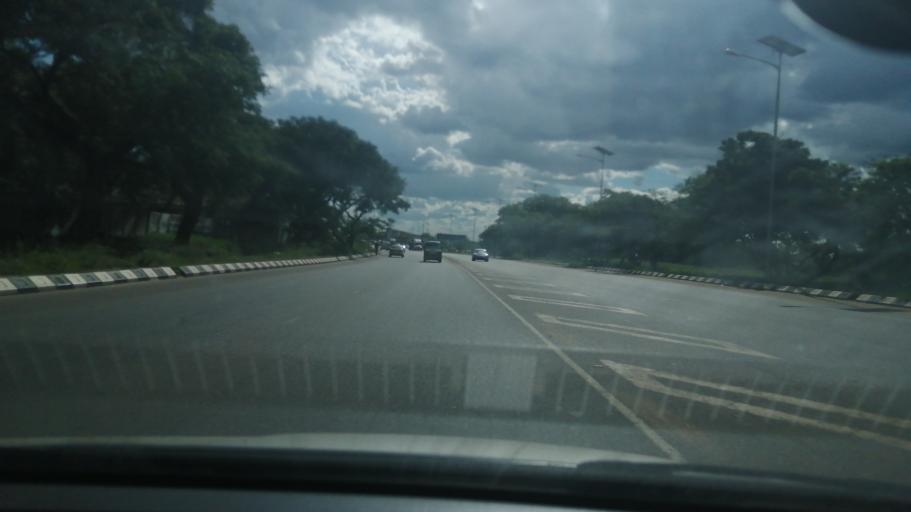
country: ZW
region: Harare
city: Harare
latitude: -17.8503
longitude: 31.0580
